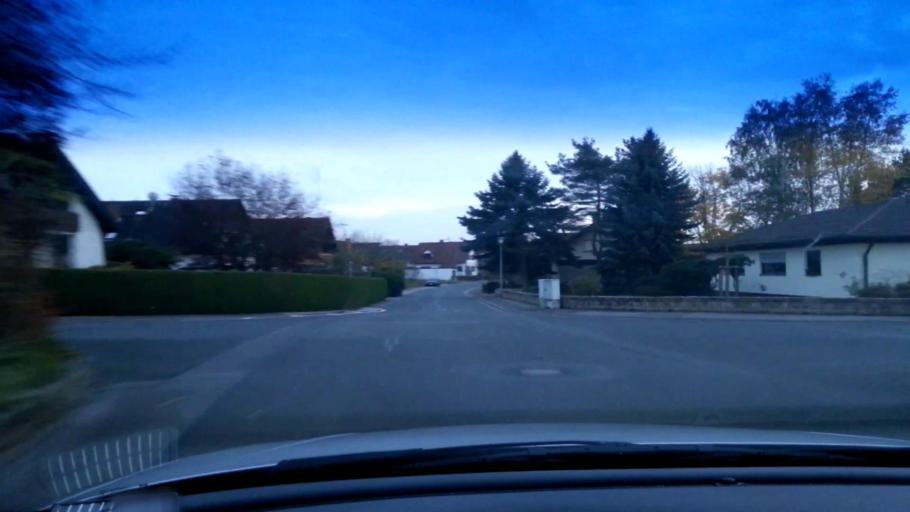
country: DE
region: Bavaria
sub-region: Upper Franconia
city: Breitengussbach
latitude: 49.9753
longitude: 10.8967
